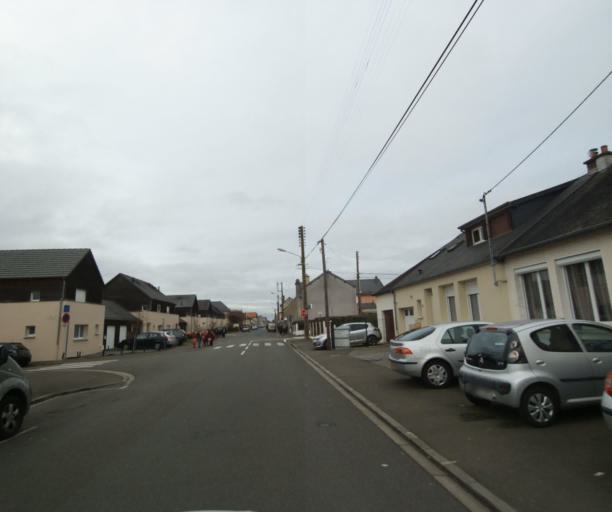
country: FR
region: Pays de la Loire
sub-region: Departement de la Sarthe
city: Le Mans
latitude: 47.9757
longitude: 0.2014
